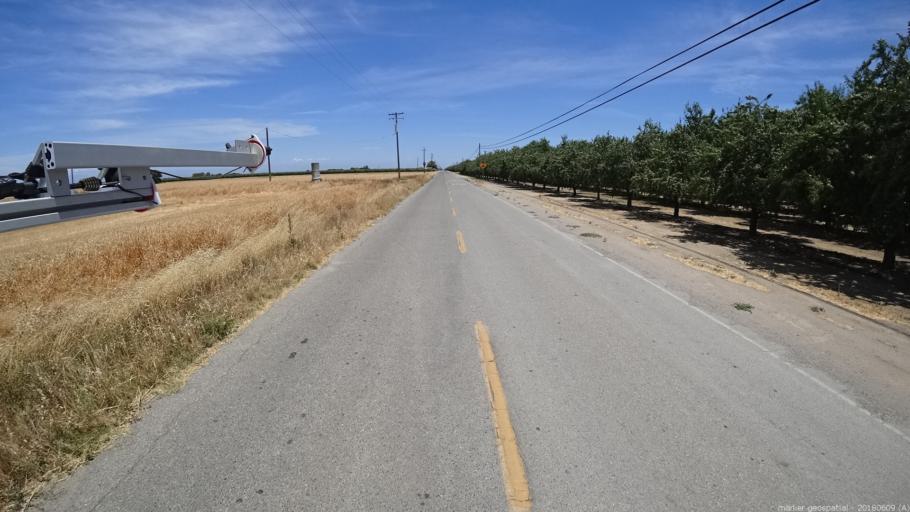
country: US
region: California
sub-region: Madera County
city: Parkwood
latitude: 36.9093
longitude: -120.0950
